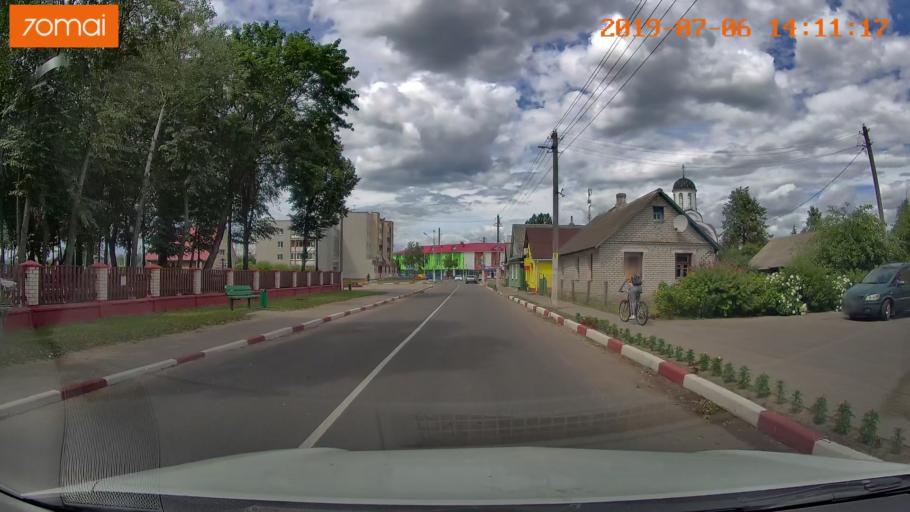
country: BY
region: Minsk
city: Ivyanyets
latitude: 53.8892
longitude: 26.7421
